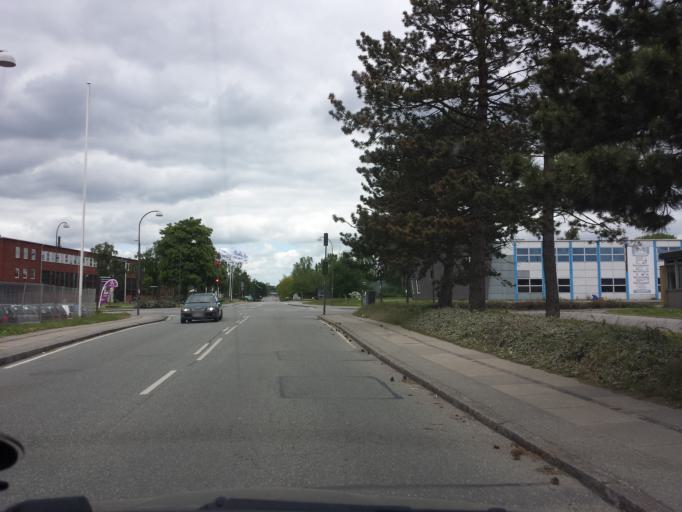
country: DK
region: Capital Region
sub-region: Herlev Kommune
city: Herlev
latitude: 55.7161
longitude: 12.4292
